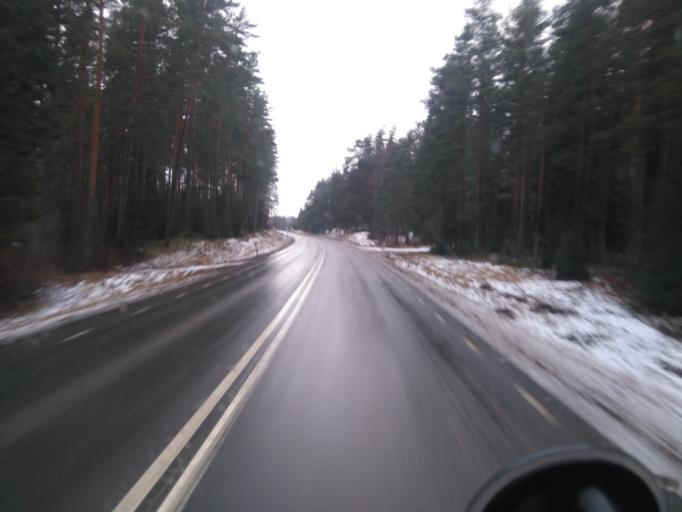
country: SE
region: Joenkoeping
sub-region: Eksjo Kommun
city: Haljarp
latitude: 57.6292
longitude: 15.4397
